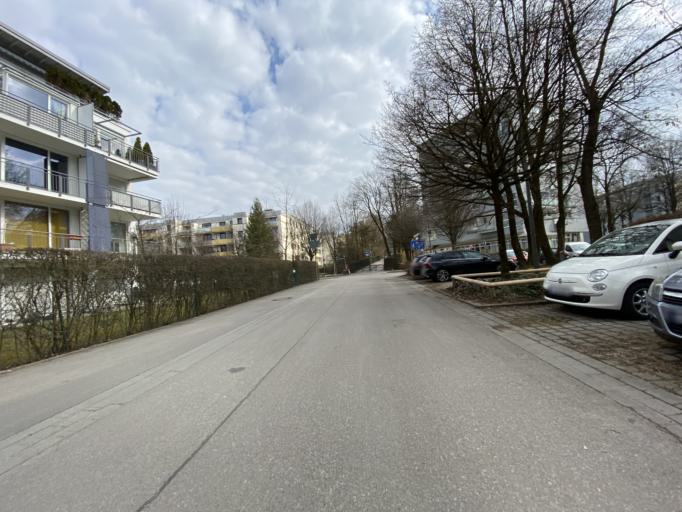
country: DE
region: Bavaria
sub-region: Upper Bavaria
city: Unterfoehring
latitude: 48.1740
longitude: 11.6321
